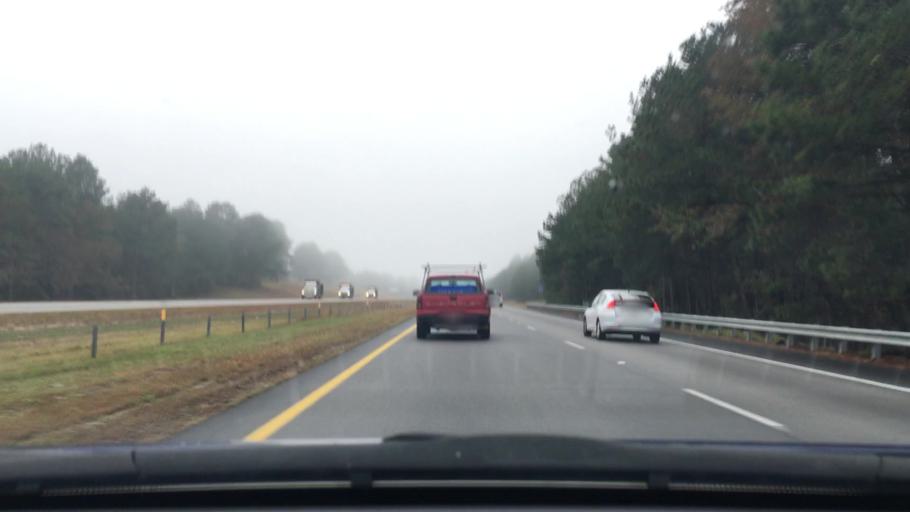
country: US
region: South Carolina
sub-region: Kershaw County
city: Camden
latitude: 34.2114
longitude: -80.4303
